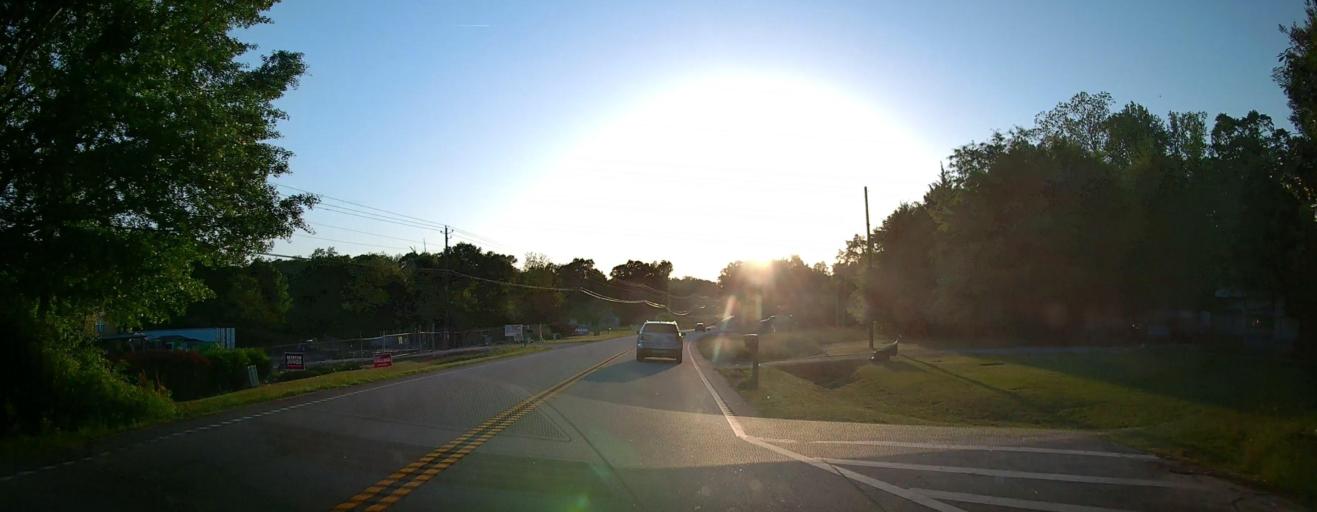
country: US
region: Georgia
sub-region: Henry County
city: McDonough
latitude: 33.4268
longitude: -84.0787
